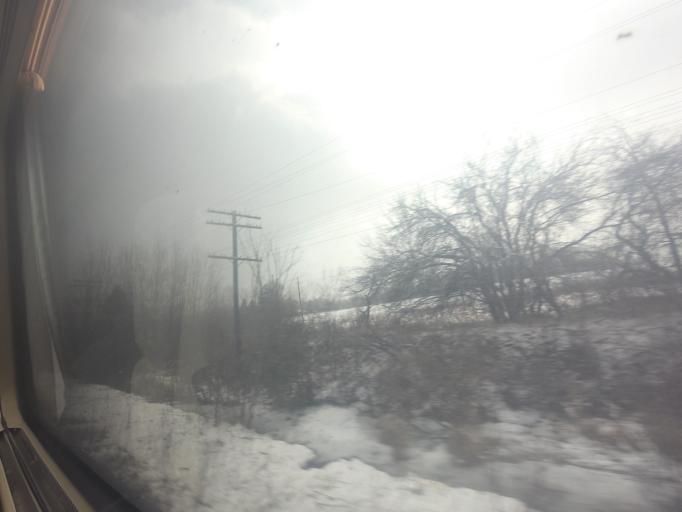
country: CA
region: Ontario
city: Cobourg
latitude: 43.9218
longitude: -78.4456
